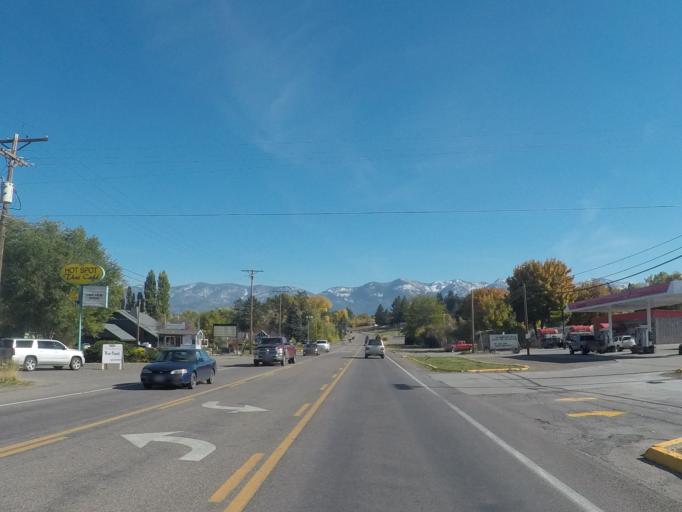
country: US
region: Montana
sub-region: Lake County
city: Polson
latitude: 47.6928
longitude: -114.1431
